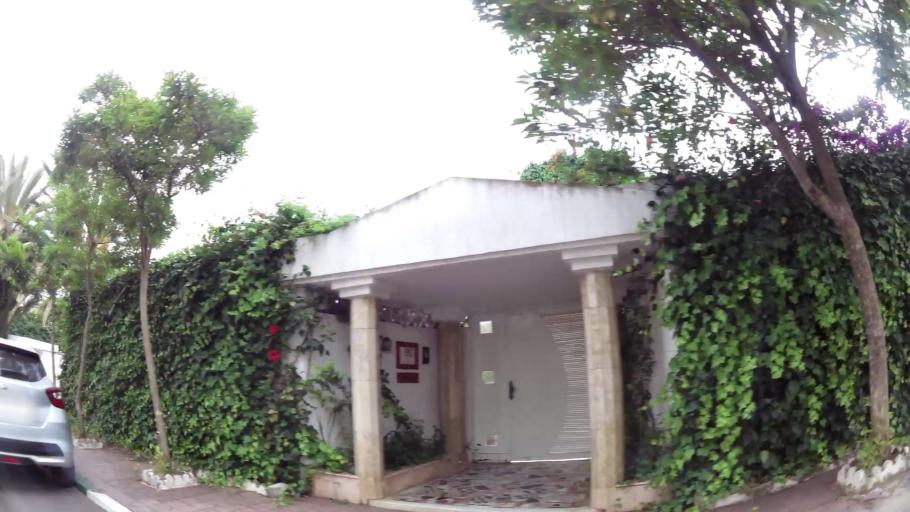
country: MA
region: Rabat-Sale-Zemmour-Zaer
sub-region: Rabat
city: Rabat
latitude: 33.9778
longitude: -6.8131
